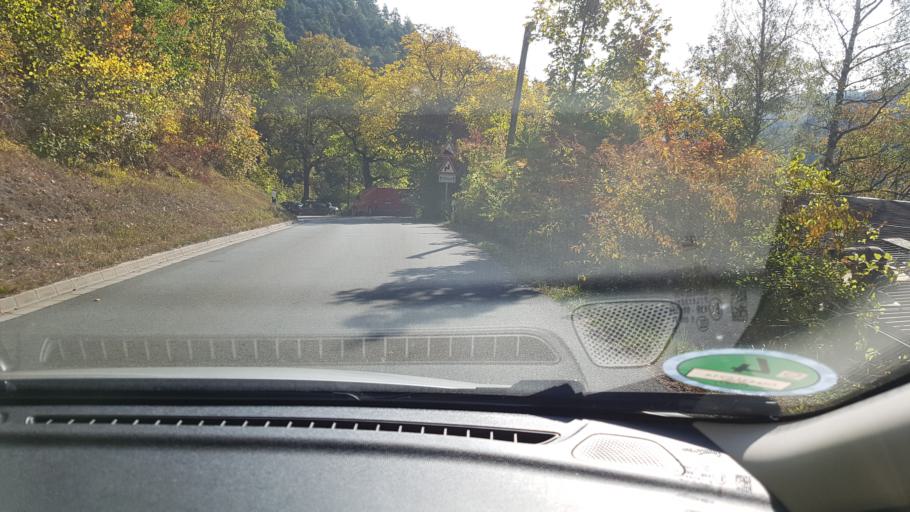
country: DE
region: Bavaria
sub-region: Upper Franconia
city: Gossweinstein
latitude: 49.8019
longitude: 11.2659
